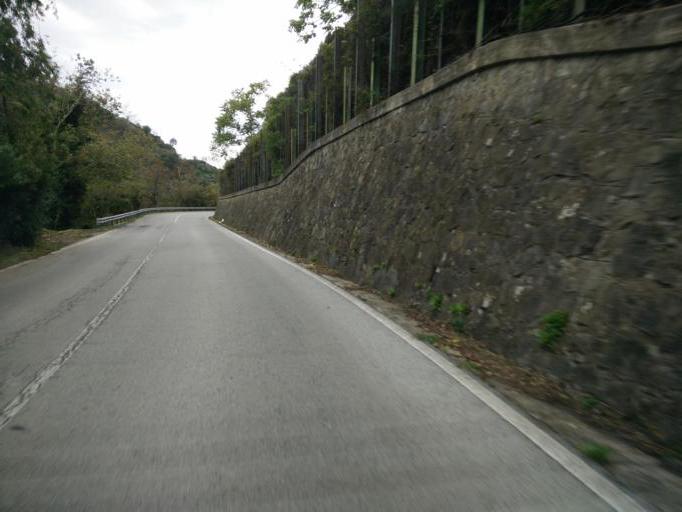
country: IT
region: Liguria
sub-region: Provincia di La Spezia
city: Riomaggiore
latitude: 44.1024
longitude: 9.7478
